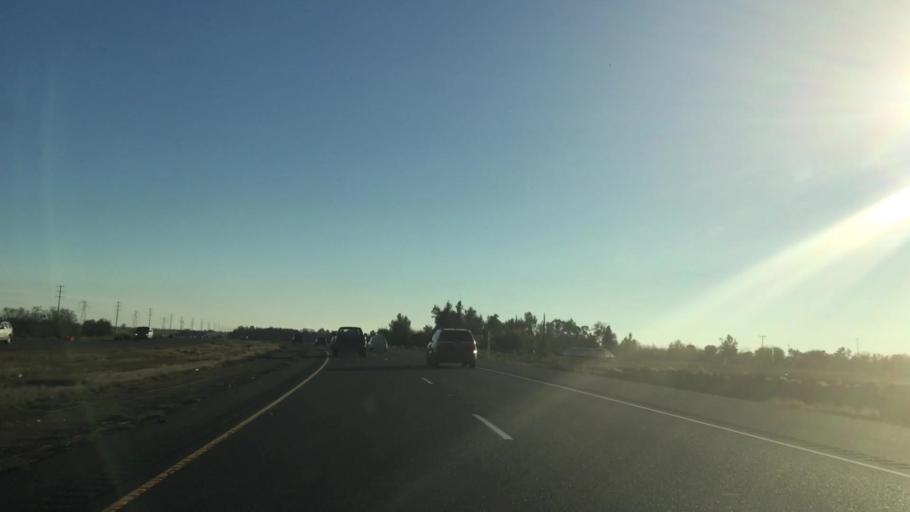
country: US
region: California
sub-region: Yuba County
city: Olivehurst
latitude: 39.0596
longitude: -121.5441
